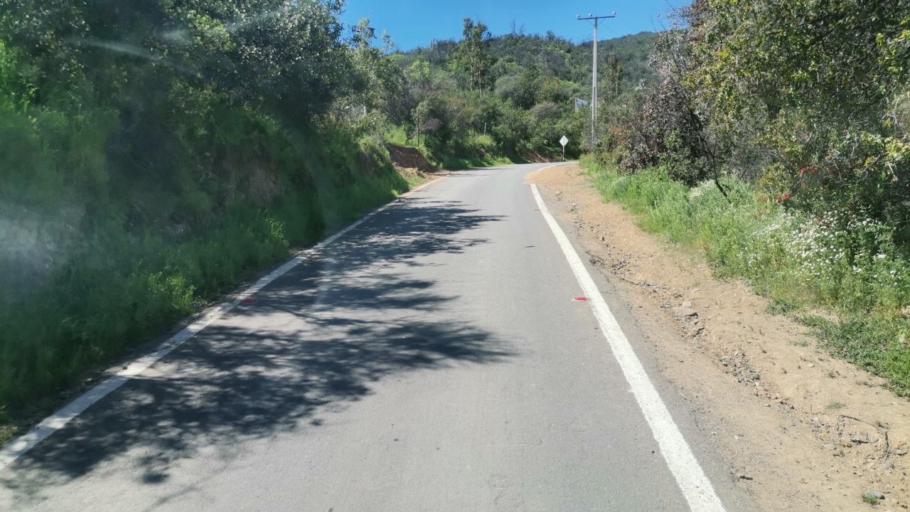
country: CL
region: Santiago Metropolitan
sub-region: Provincia de Chacabuco
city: Lampa
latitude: -33.1948
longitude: -71.0920
